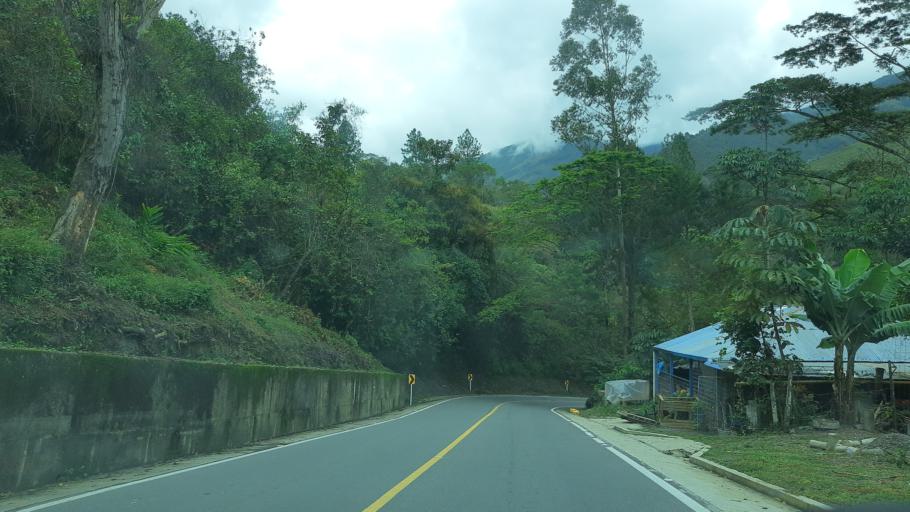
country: CO
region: Boyaca
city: Chivor
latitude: 4.9500
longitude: -73.3052
